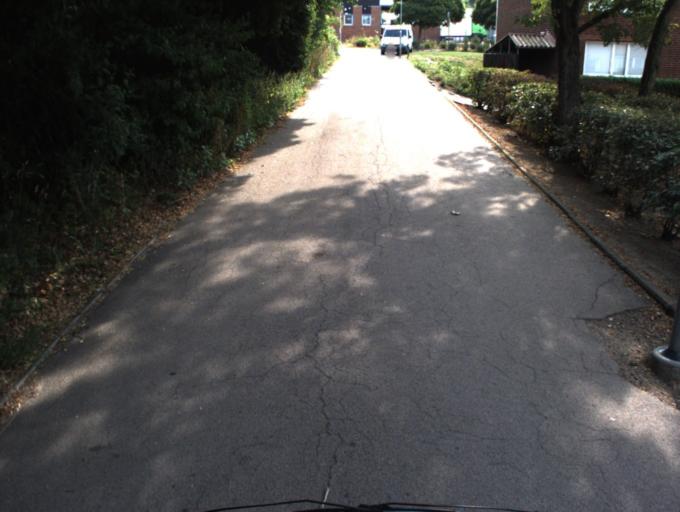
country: SE
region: Skane
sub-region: Helsingborg
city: Helsingborg
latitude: 56.0454
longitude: 12.7439
